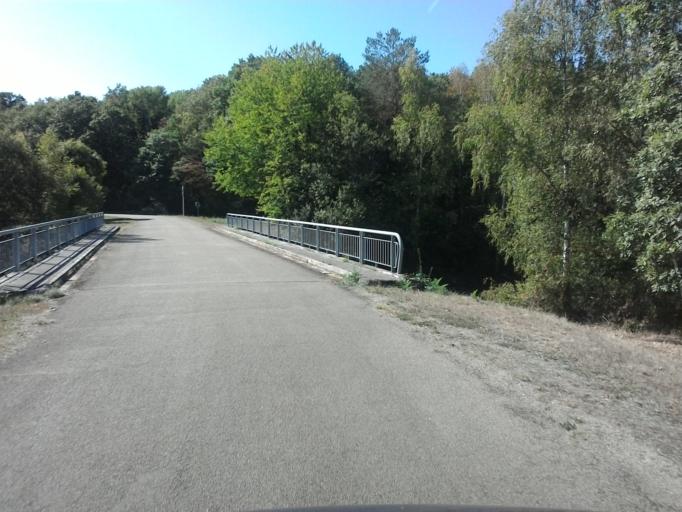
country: FR
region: Bourgogne
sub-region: Departement de la Cote-d'Or
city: Semur-en-Auxois
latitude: 47.4704
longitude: 4.3533
